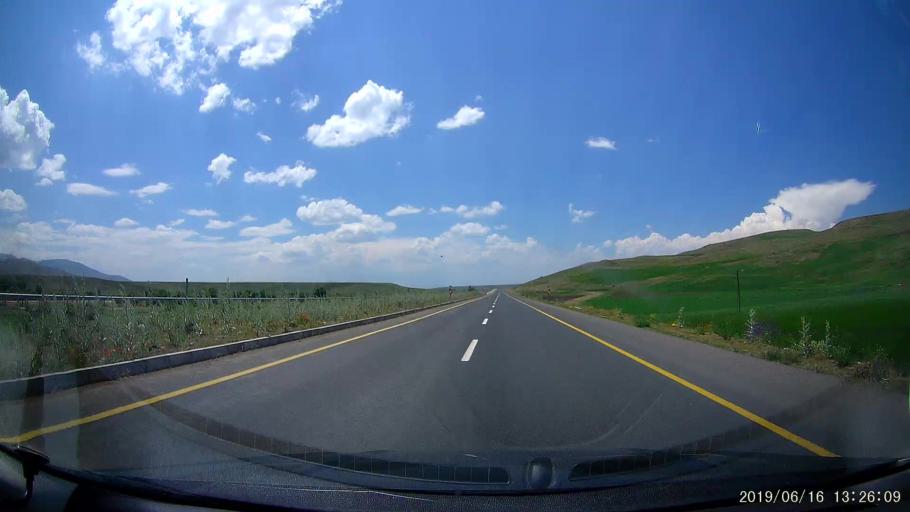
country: TR
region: Agri
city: Taslicay
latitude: 39.6574
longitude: 43.3348
